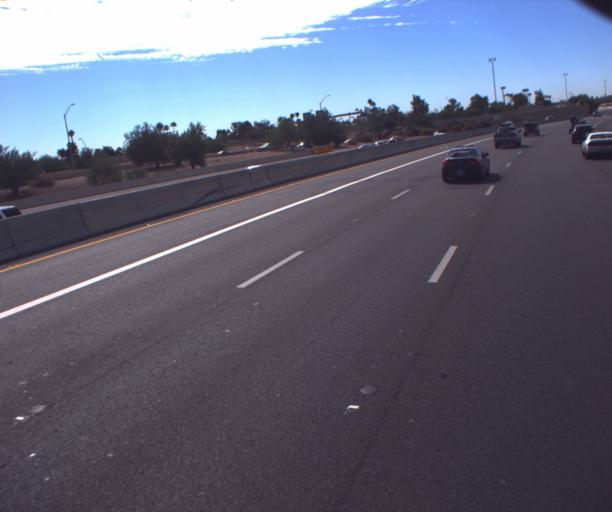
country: US
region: Arizona
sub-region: Maricopa County
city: Tempe
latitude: 33.3842
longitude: -111.8914
